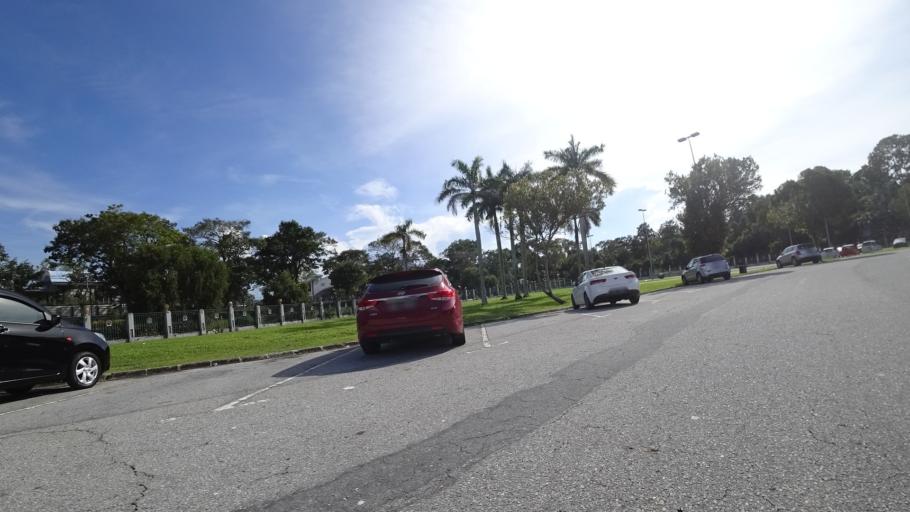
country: BN
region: Brunei and Muara
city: Bandar Seri Begawan
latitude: 4.9353
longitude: 114.8337
